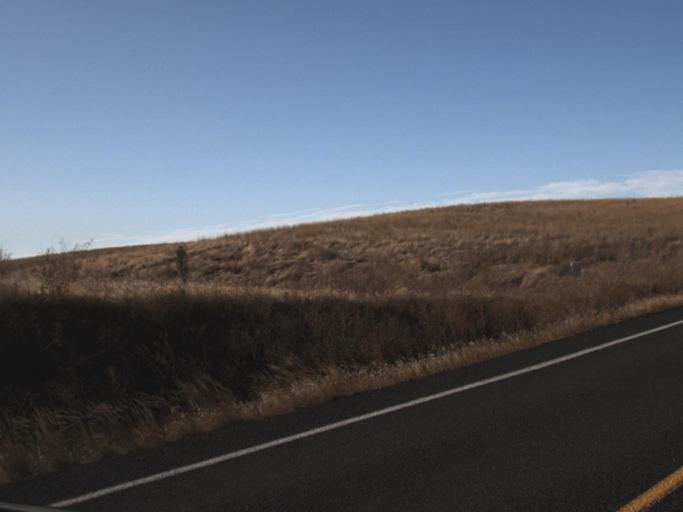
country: US
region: Washington
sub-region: Walla Walla County
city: Garrett
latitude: 46.2922
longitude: -118.5584
